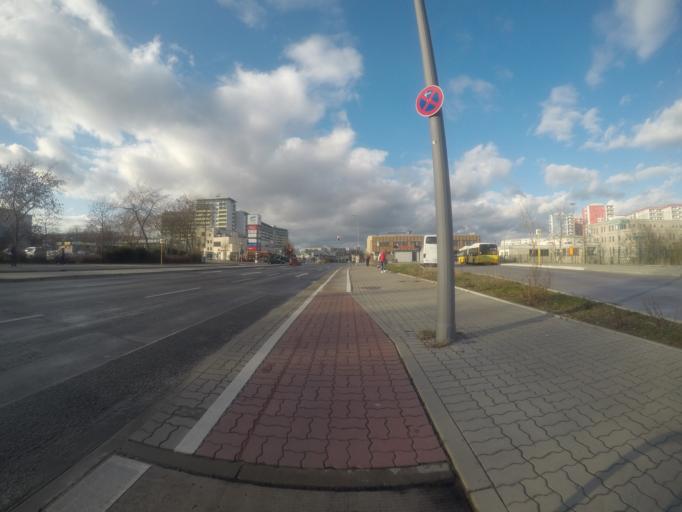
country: DE
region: Berlin
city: Kaulsdorf
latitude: 52.5201
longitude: 13.5884
